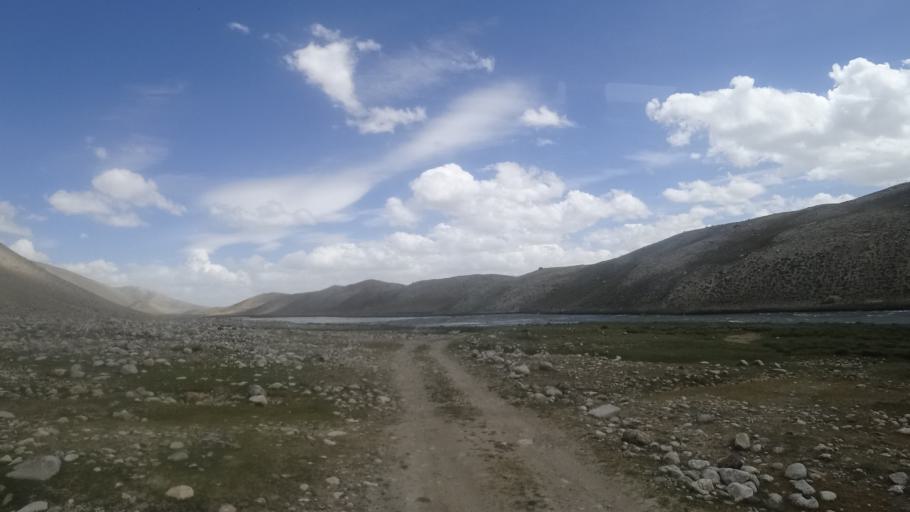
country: TJ
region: Gorno-Badakhshan
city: Murghob
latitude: 37.4748
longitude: 73.4551
